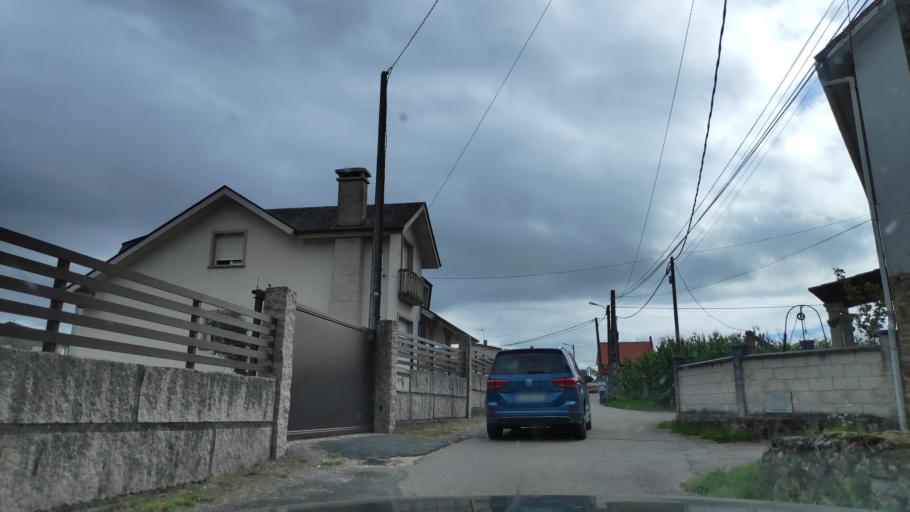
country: ES
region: Galicia
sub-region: Provincia da Coruna
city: Rianxo
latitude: 42.6708
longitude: -8.8154
